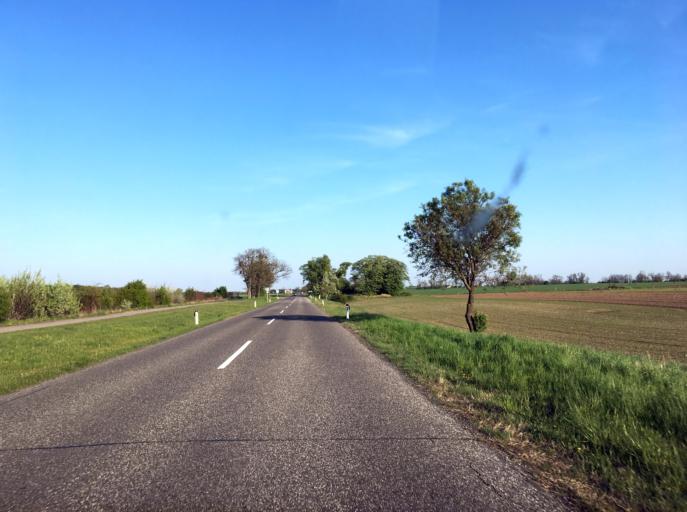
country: AT
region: Burgenland
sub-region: Politischer Bezirk Neusiedl am See
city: Kittsee
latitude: 48.0790
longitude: 17.0767
